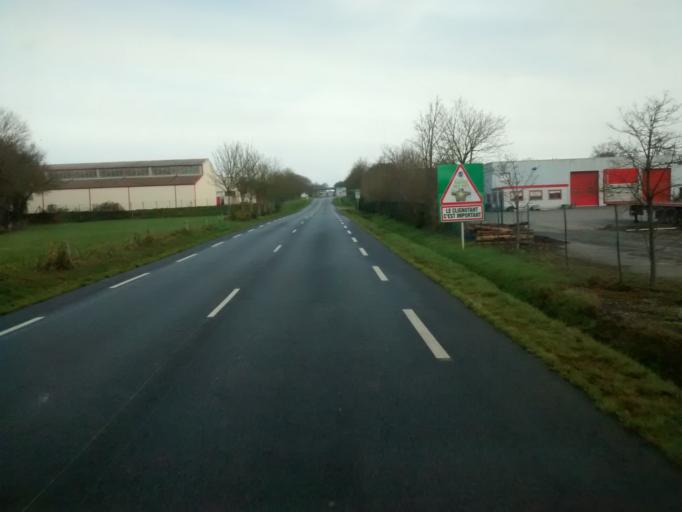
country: FR
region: Brittany
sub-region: Departement du Morbihan
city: Malestroit
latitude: 47.8466
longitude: -2.4170
